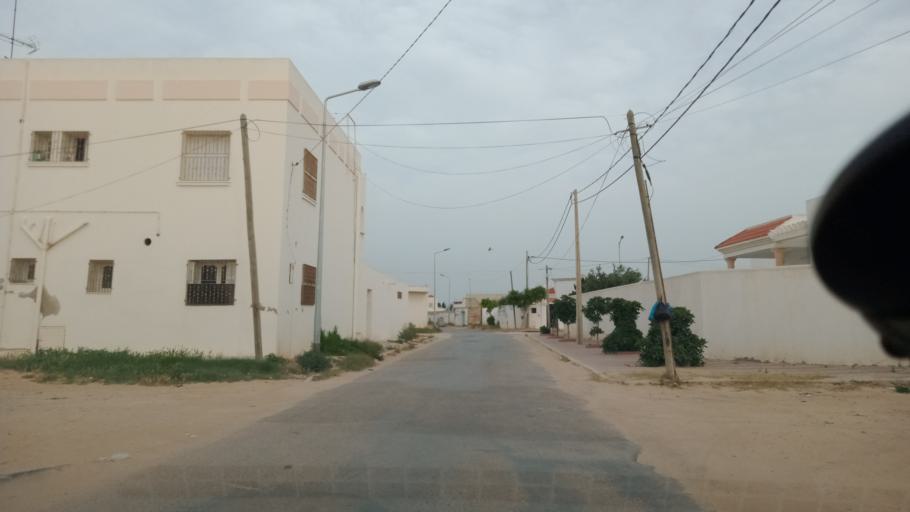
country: TN
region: Safaqis
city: Al Qarmadah
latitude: 34.7898
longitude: 10.7727
